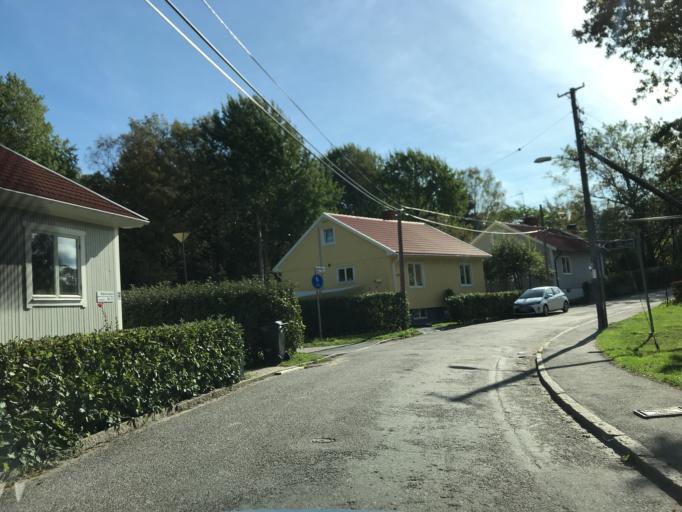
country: SE
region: Stockholm
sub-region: Huddinge Kommun
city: Segeltorp
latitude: 59.2772
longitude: 17.9707
